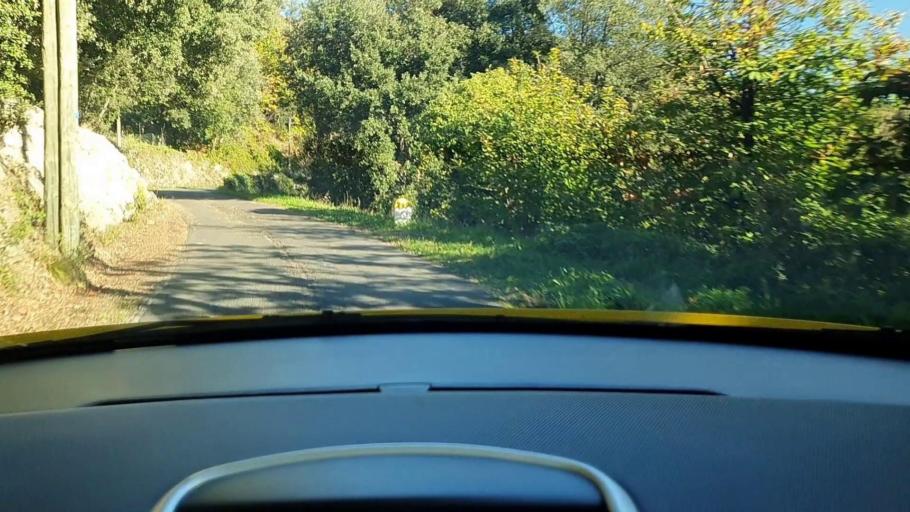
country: FR
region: Languedoc-Roussillon
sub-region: Departement du Gard
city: Sumene
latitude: 44.0220
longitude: 3.7629
